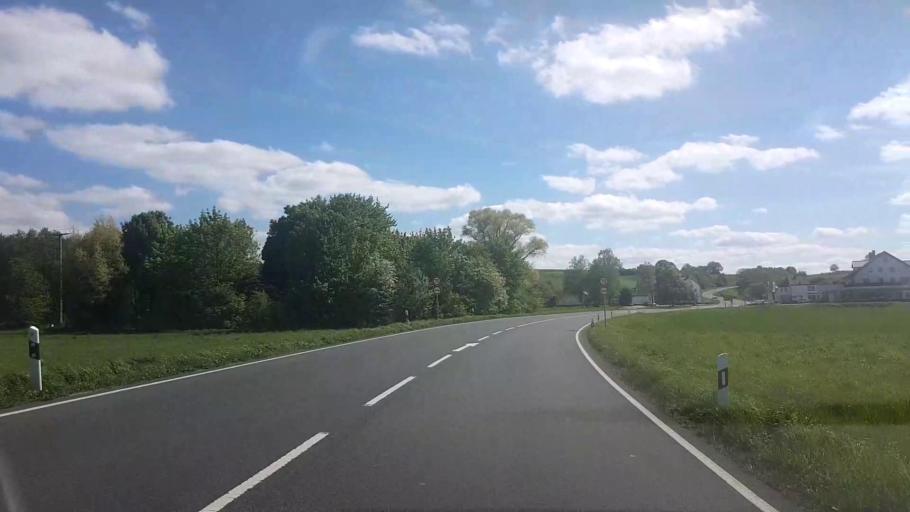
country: DE
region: Bavaria
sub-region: Regierungsbezirk Unterfranken
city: Untermerzbach
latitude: 50.0822
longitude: 10.8675
